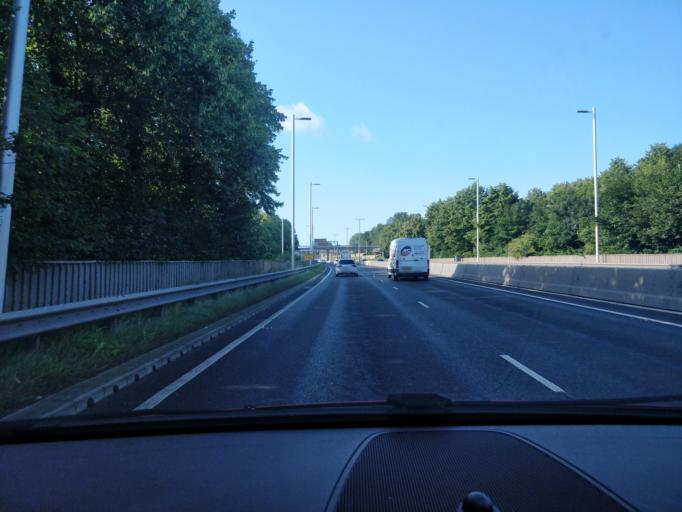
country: GB
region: England
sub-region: Borough of Halton
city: Halton
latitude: 53.3362
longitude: -2.7039
